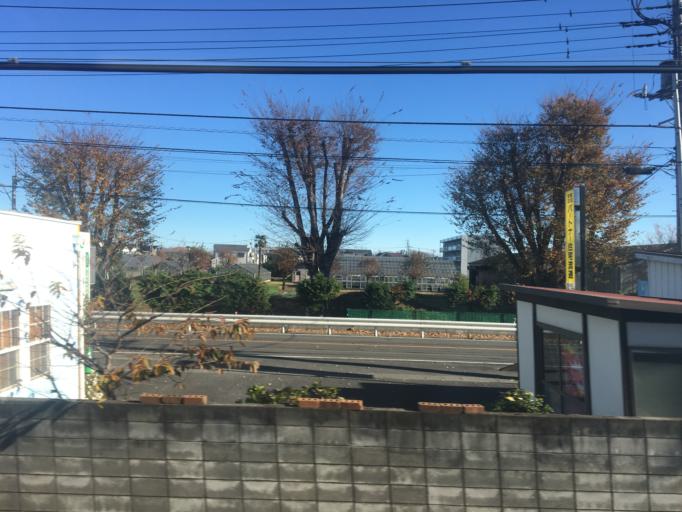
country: JP
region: Saitama
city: Sakado
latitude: 35.9533
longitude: 139.4035
